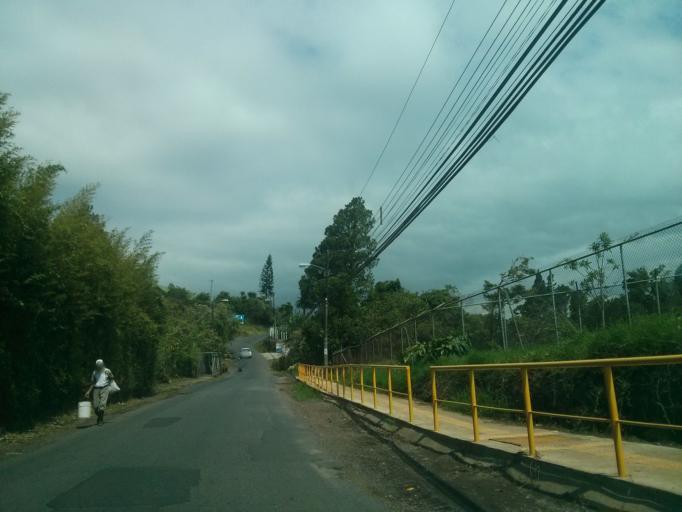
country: CR
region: Heredia
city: Angeles
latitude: 10.0187
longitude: -84.0359
